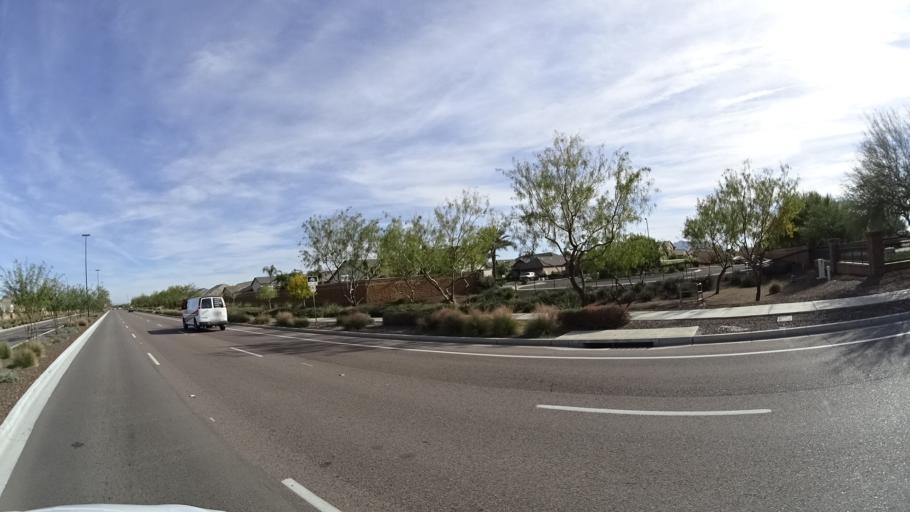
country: US
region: Arizona
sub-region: Maricopa County
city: Gilbert
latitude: 33.2776
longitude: -111.7287
